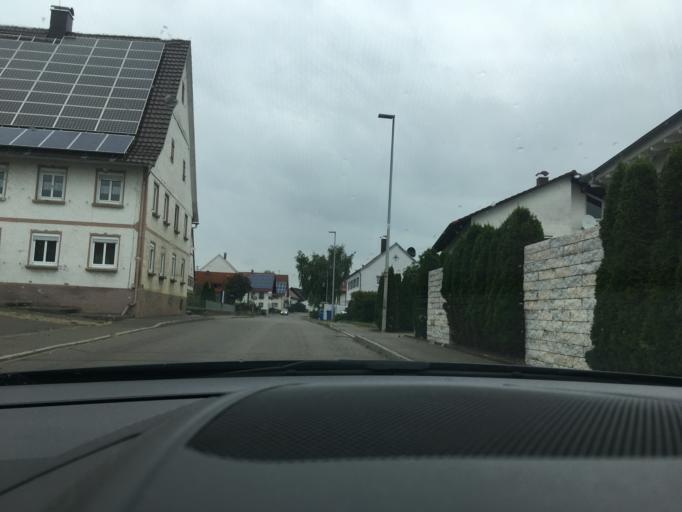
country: DE
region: Bavaria
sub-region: Swabia
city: Heimertingen
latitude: 48.0436
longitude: 10.1224
